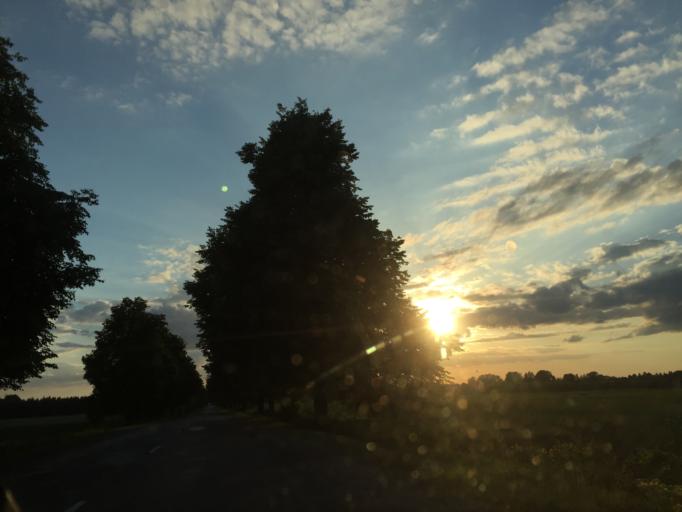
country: LV
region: Sigulda
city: Sigulda
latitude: 57.1390
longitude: 24.8800
